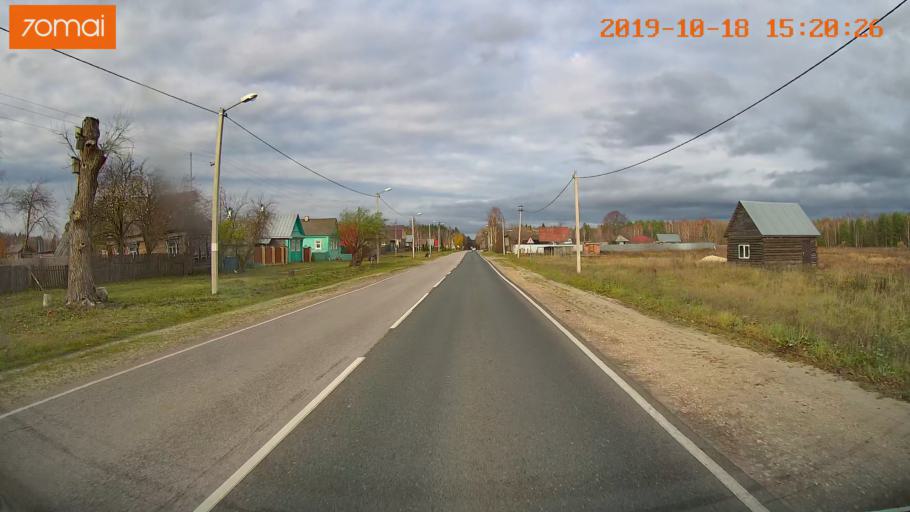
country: RU
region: Vladimir
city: Anopino
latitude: 55.6868
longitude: 40.7446
